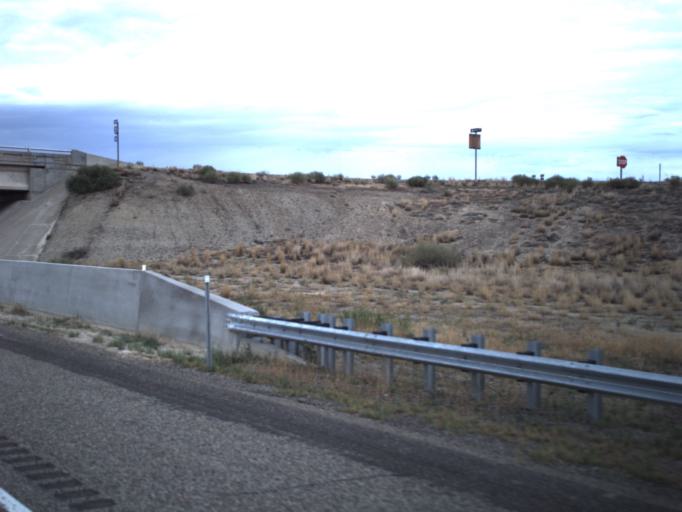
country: US
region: Colorado
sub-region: Mesa County
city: Loma
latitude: 39.1132
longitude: -109.1843
